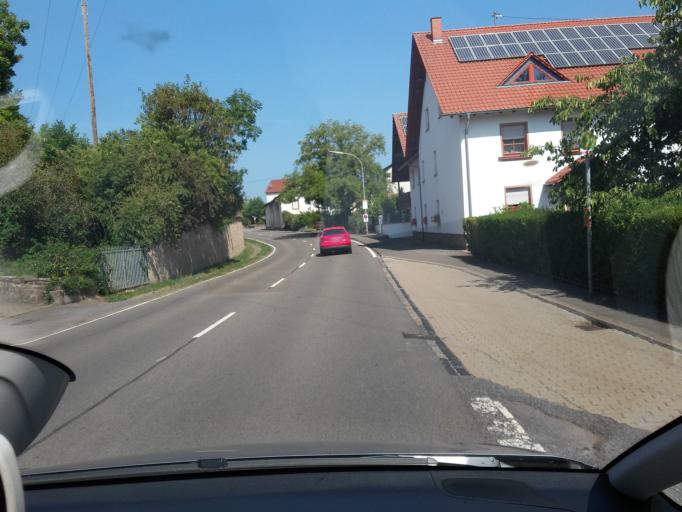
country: DE
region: Saarland
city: Mettlach
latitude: 49.4575
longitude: 6.5971
